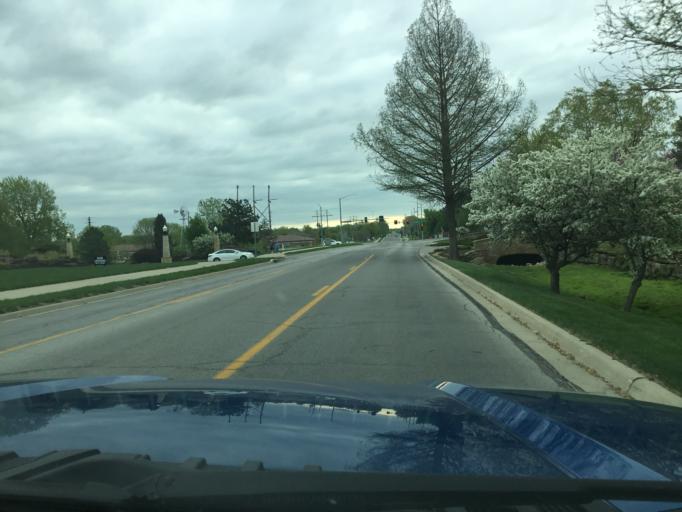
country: US
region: Kansas
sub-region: Douglas County
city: Lawrence
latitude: 38.9861
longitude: -95.2810
